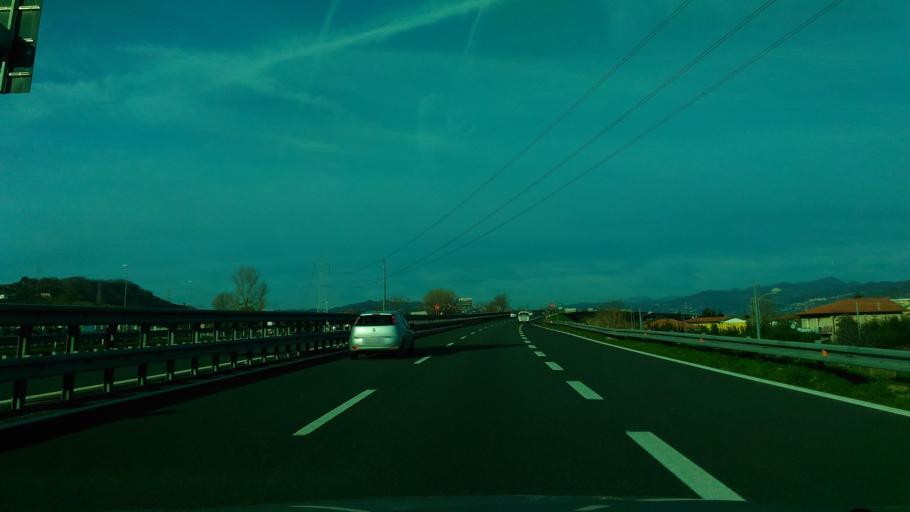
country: IT
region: Liguria
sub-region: Provincia di La Spezia
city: Sarzana
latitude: 44.1027
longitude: 9.9497
